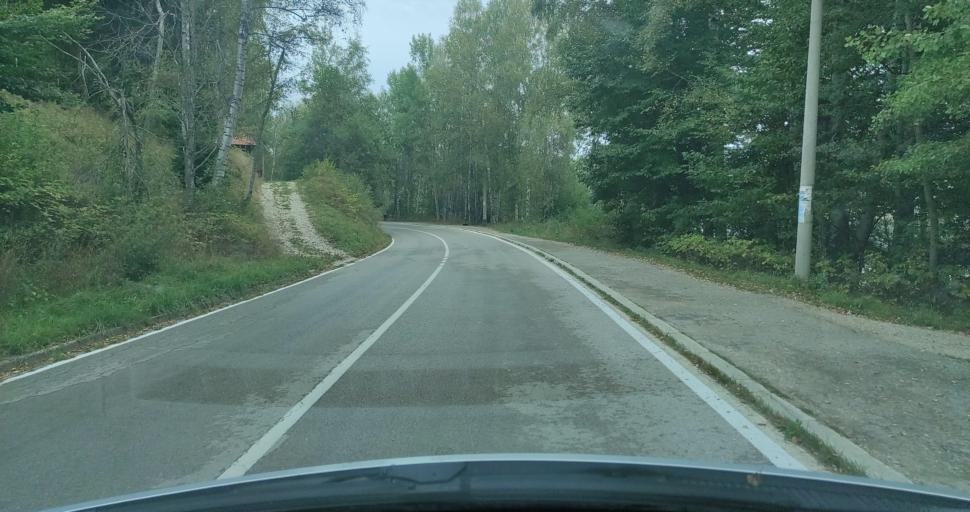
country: RS
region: Central Serbia
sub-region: Jablanicki Okrug
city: Crna Trava
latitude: 42.7431
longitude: 22.3291
